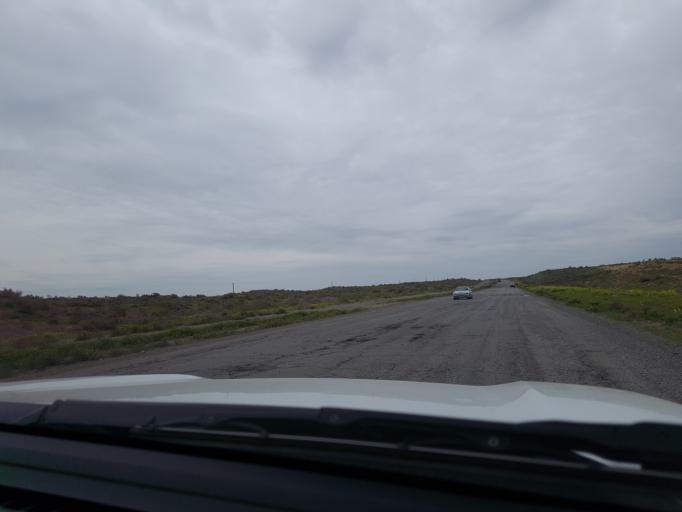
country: TM
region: Mary
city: Bayramaly
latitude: 37.9000
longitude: 62.6177
